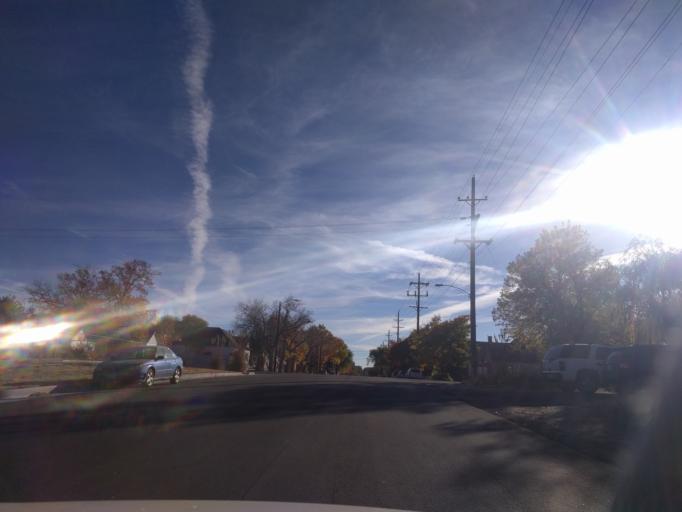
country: US
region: Colorado
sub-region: El Paso County
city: Colorado Springs
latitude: 38.8233
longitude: -104.8284
